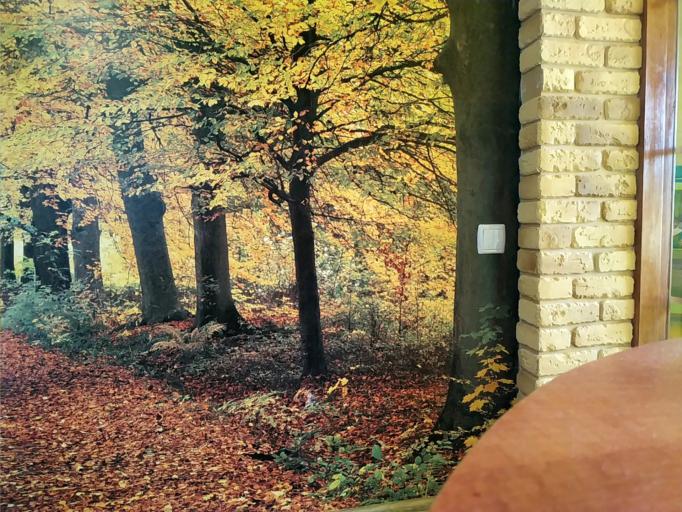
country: RU
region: Novgorod
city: Sol'tsy
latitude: 57.9042
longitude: 30.2229
